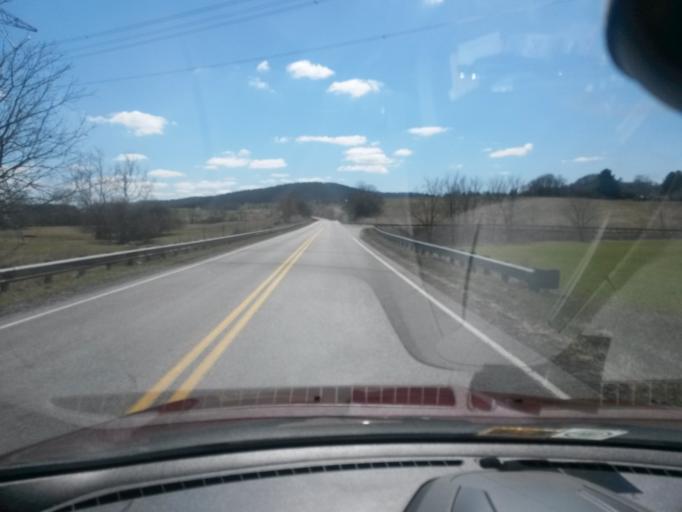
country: US
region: Virginia
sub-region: Augusta County
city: Jolivue
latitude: 38.0620
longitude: -79.0697
